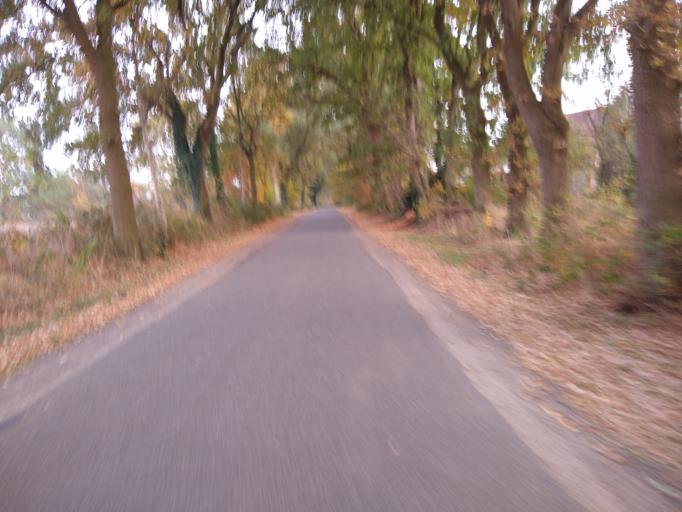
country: DE
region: Lower Saxony
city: Rastede
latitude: 53.2110
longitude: 8.2355
